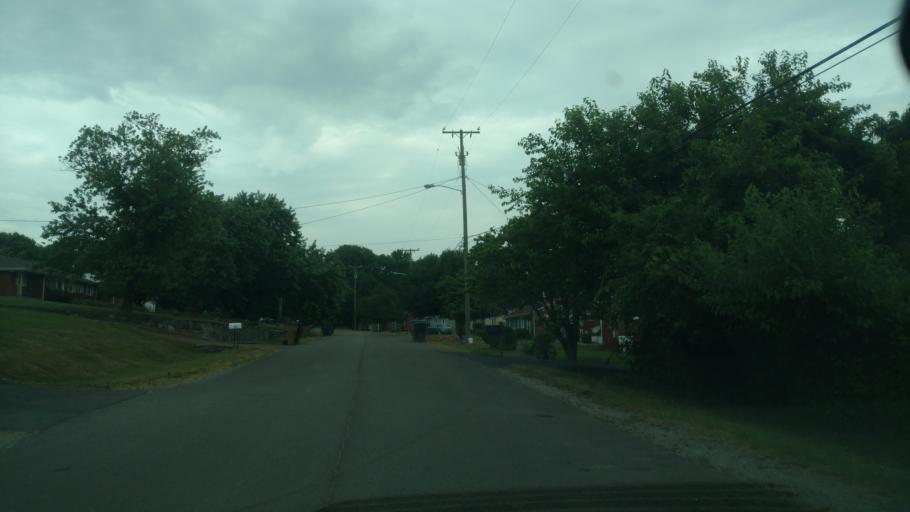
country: US
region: Tennessee
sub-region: Davidson County
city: Nashville
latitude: 36.1993
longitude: -86.7081
